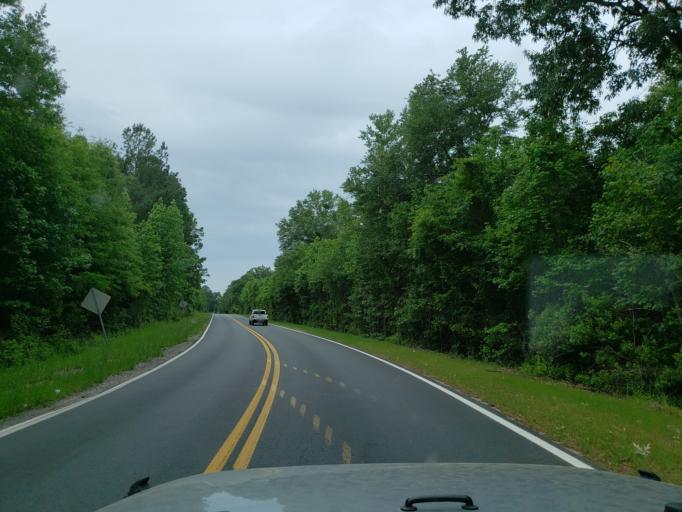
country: US
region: Georgia
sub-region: Chatham County
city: Port Wentworth
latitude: 32.1852
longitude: -81.1948
